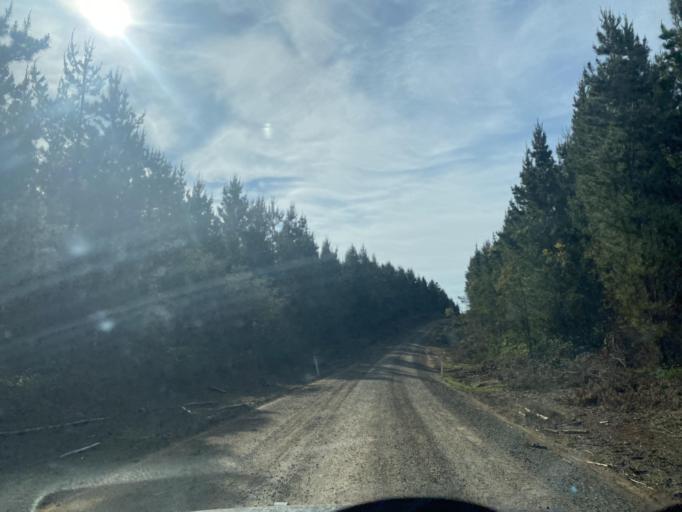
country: AU
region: Victoria
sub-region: Mansfield
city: Mansfield
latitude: -36.8764
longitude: 146.1850
